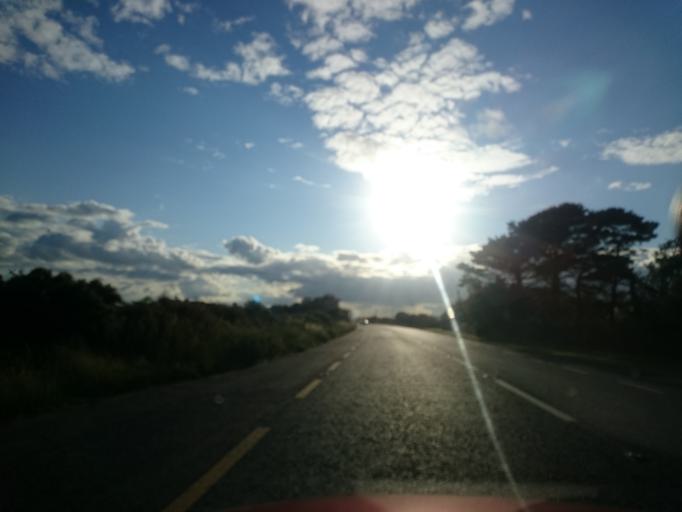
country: IE
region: Leinster
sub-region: Loch Garman
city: Ballygerry
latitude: 52.2445
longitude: -6.3680
